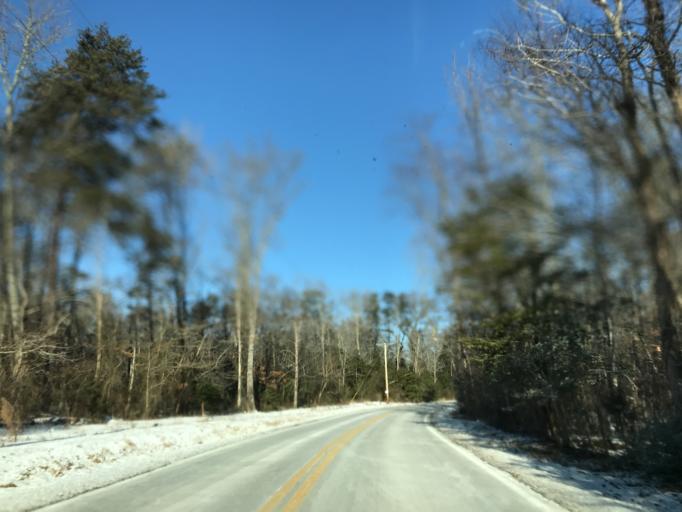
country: US
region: Maryland
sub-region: Charles County
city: La Plata
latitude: 38.4231
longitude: -76.9312
